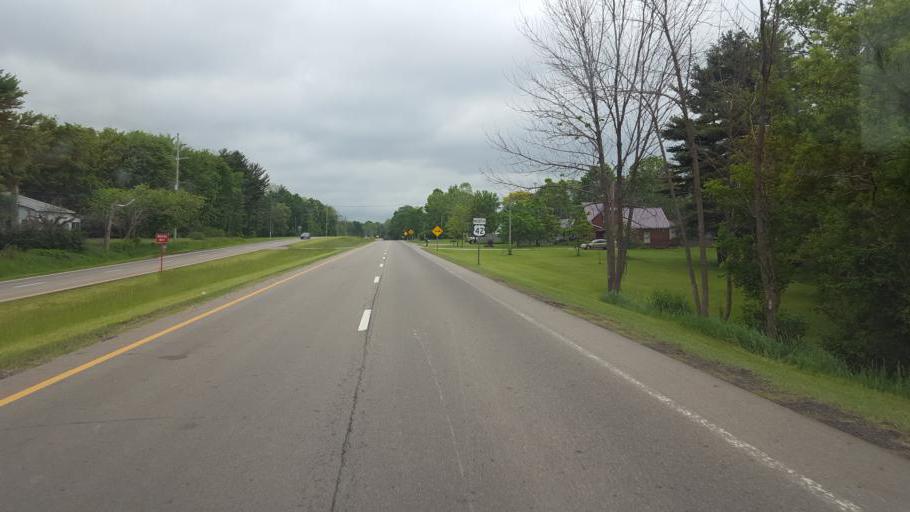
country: US
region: Ohio
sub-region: Wayne County
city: West Salem
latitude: 40.9591
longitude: -82.1278
